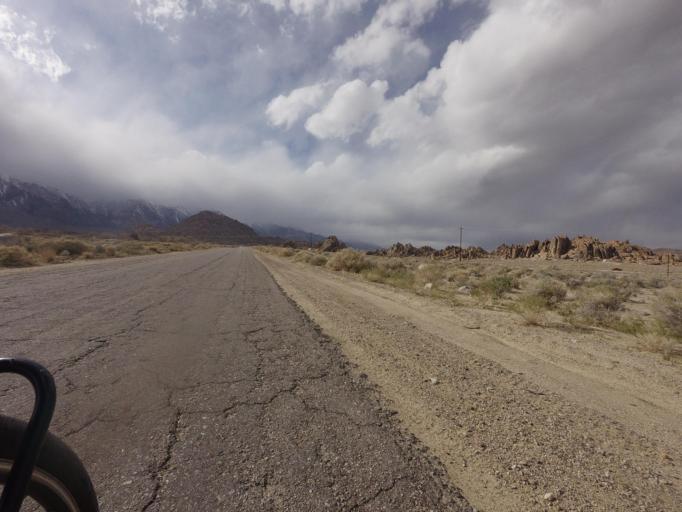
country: US
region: California
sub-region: Inyo County
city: Lone Pine
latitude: 36.5966
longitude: -118.1095
